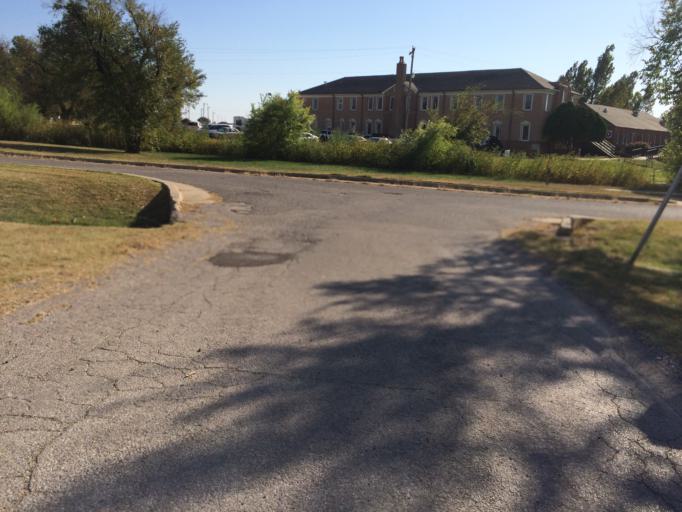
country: US
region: Oklahoma
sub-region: Cleveland County
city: Norman
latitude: 35.2283
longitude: -97.4244
